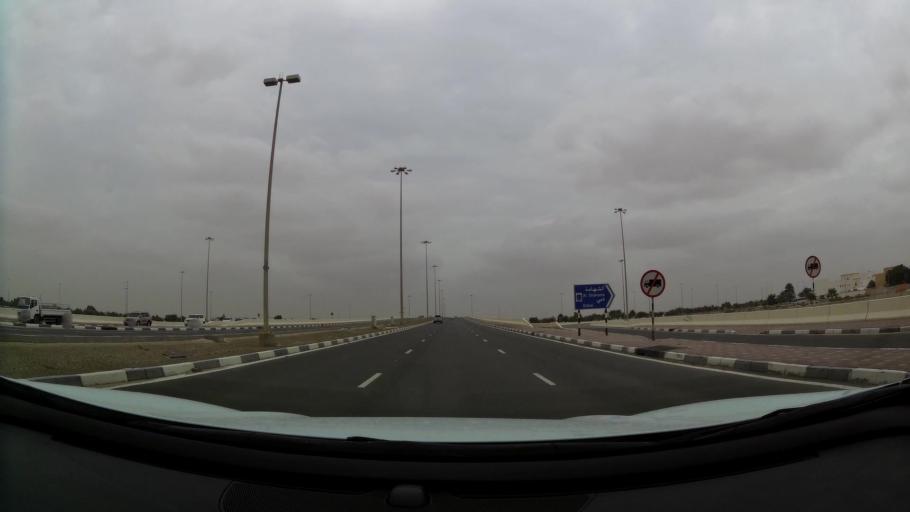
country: AE
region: Abu Dhabi
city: Abu Dhabi
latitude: 24.3672
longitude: 54.6573
